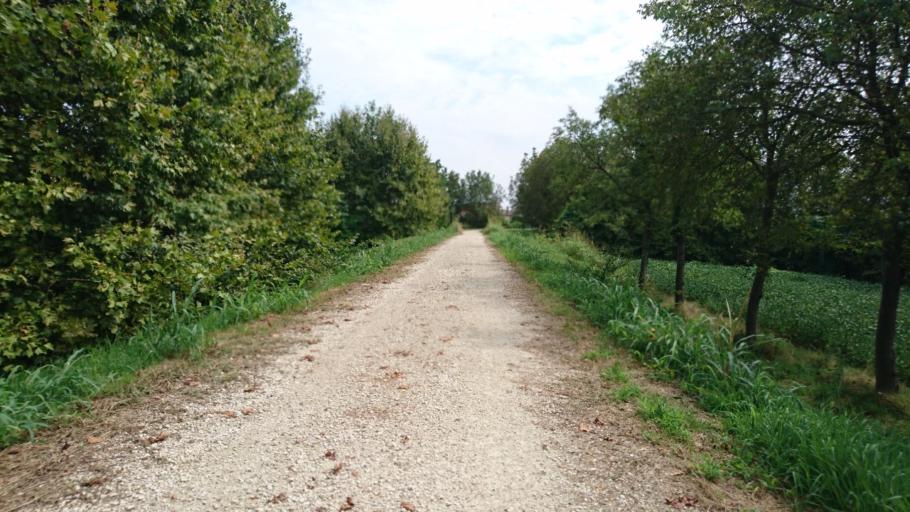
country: IT
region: Veneto
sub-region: Provincia di Vicenza
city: Longare
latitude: 45.4751
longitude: 11.6218
